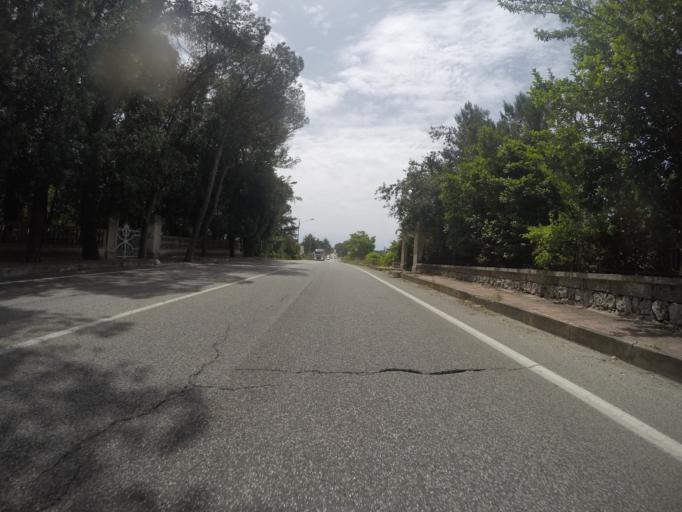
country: IT
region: Apulia
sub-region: Provincia di Taranto
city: Martina Franca
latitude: 40.6873
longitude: 17.3331
